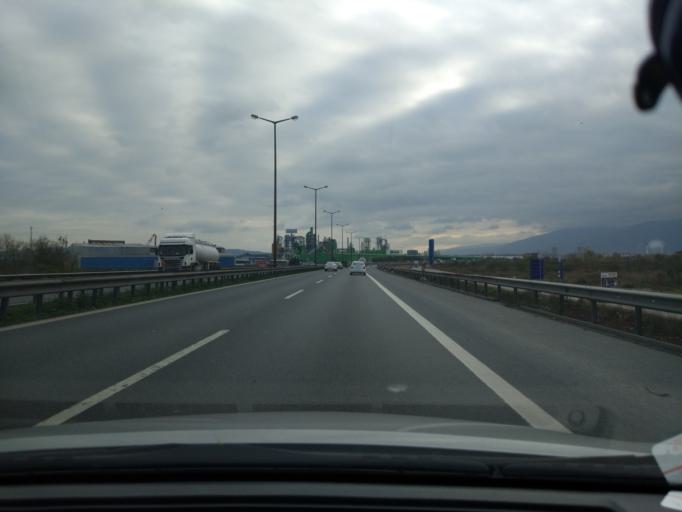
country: TR
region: Kocaeli
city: Kosekoy
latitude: 40.7653
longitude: 30.0250
